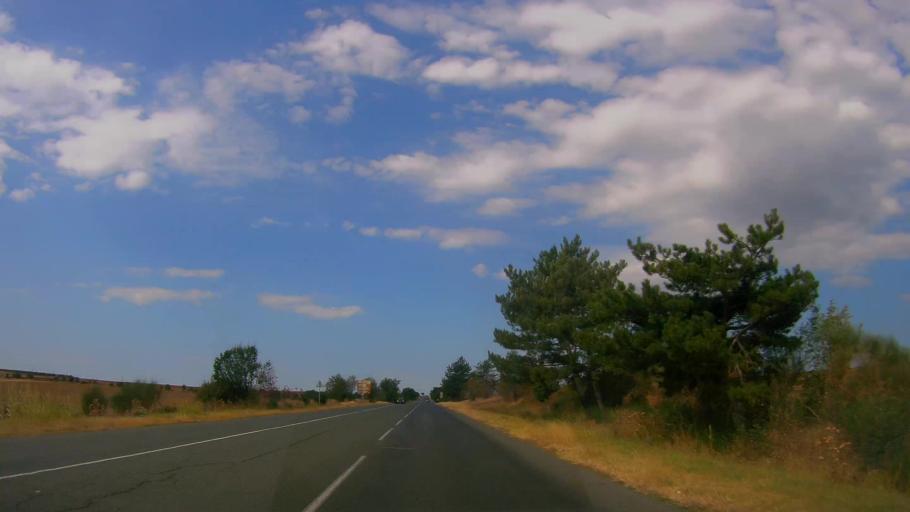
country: BG
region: Burgas
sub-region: Obshtina Aytos
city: Aytos
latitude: 42.6968
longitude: 27.1965
